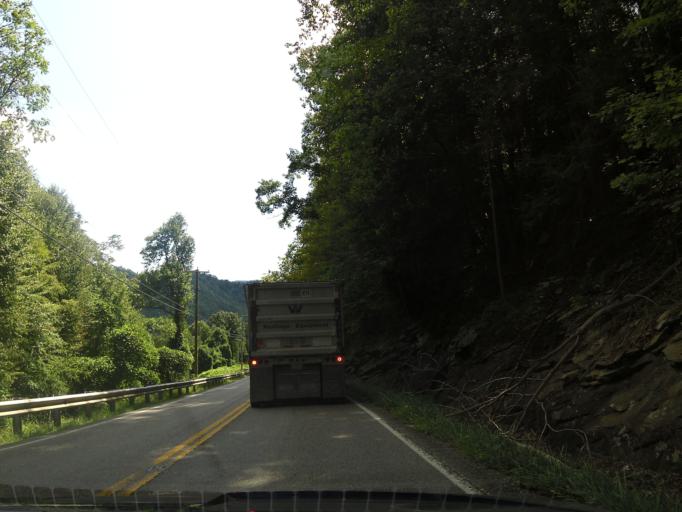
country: US
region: Kentucky
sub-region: Harlan County
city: Harlan
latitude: 36.8749
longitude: -83.3206
